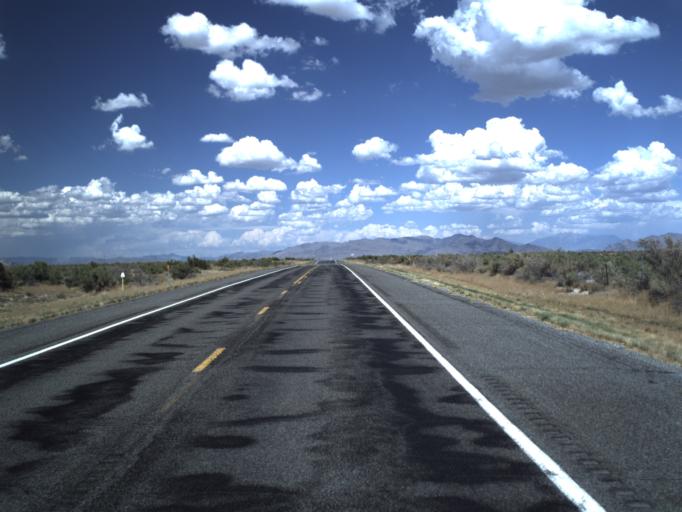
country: US
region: Utah
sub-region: Millard County
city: Delta
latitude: 39.4119
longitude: -112.4862
